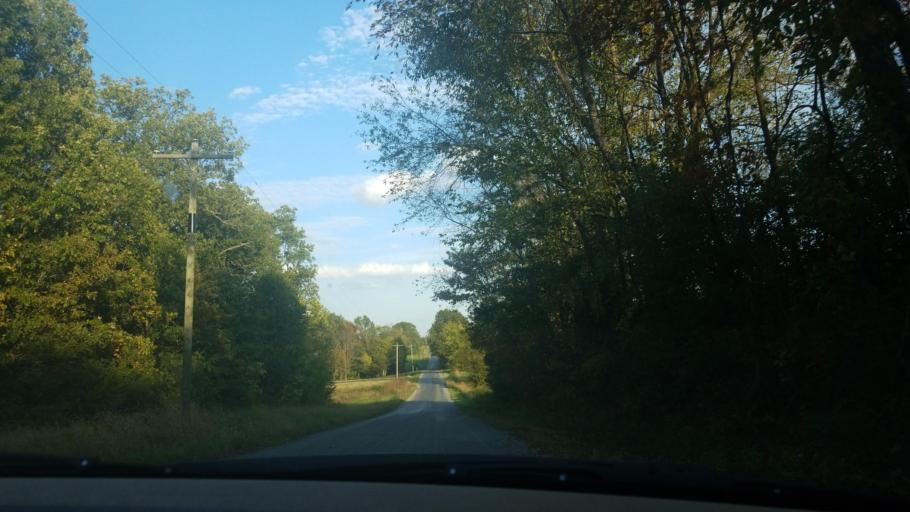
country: US
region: Illinois
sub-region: Saline County
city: Carrier Mills
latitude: 37.8050
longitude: -88.6631
